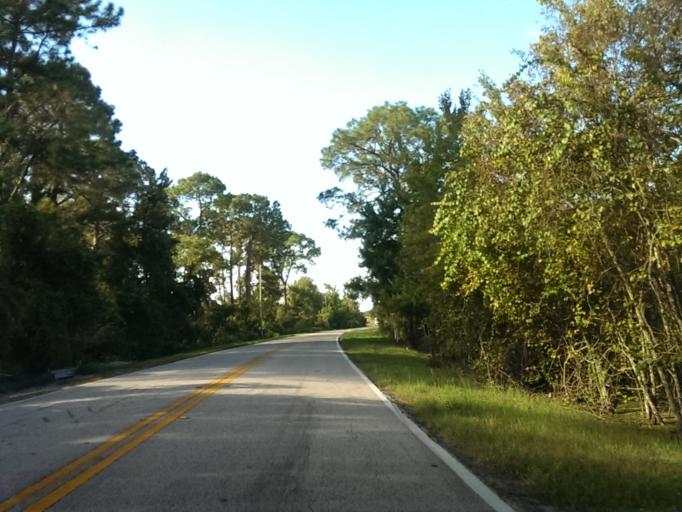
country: US
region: Florida
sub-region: Polk County
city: Citrus Ridge
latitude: 28.4068
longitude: -81.6360
